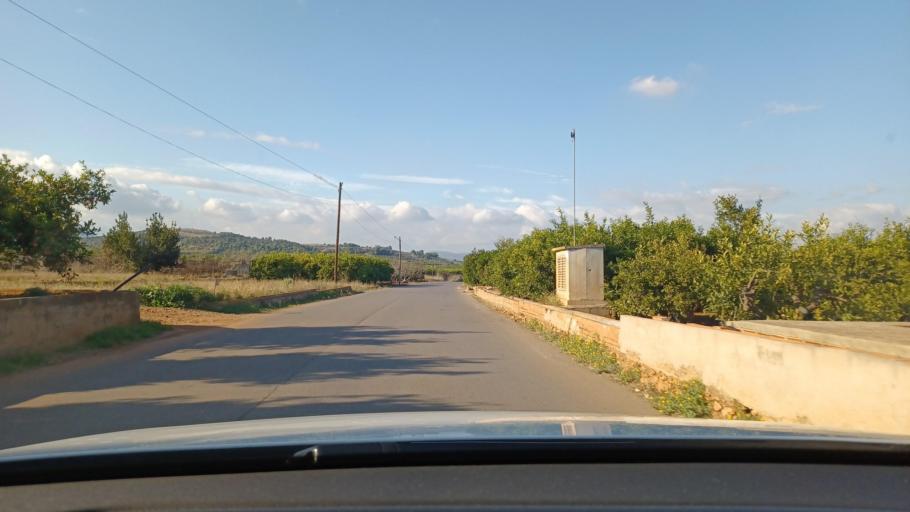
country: ES
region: Valencia
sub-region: Provincia de Castello
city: Betxi
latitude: 39.9350
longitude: -0.2056
